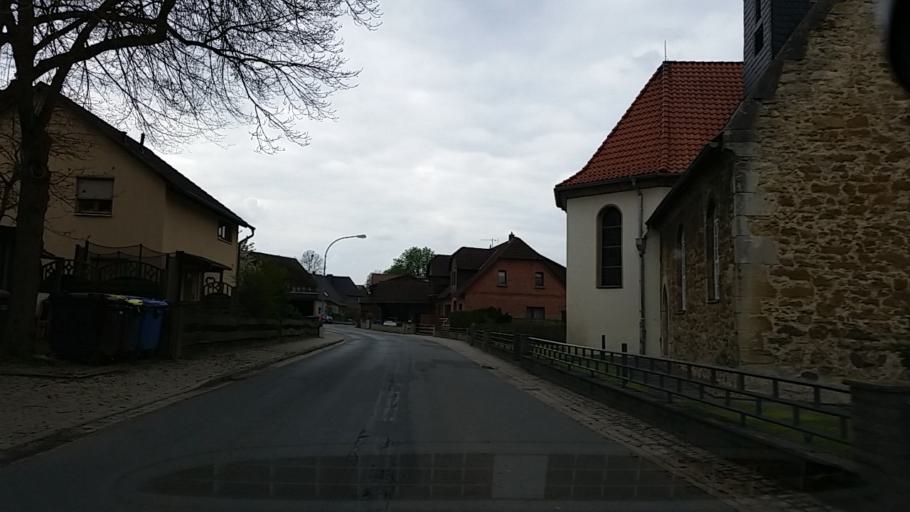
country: DE
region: Lower Saxony
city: Rotgesbuttel
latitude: 52.4168
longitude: 10.5277
